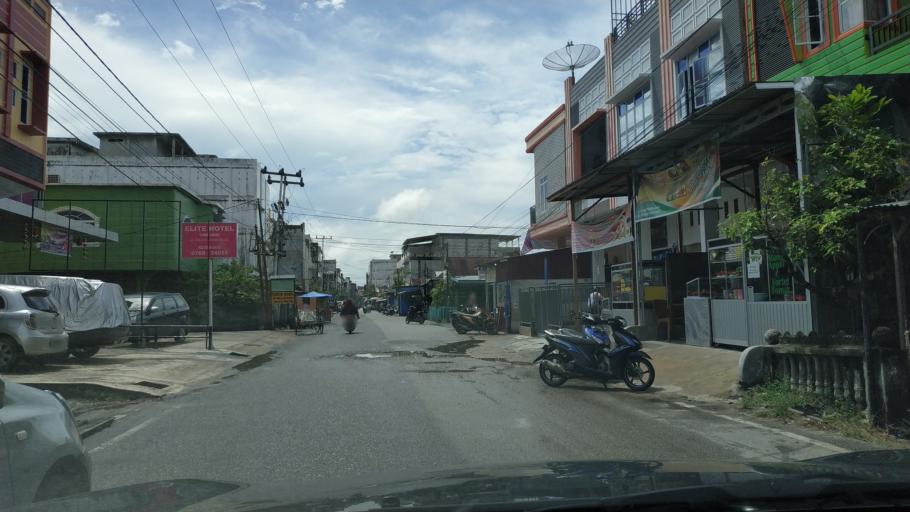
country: ID
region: Riau
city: Tembilahan
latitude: -0.3238
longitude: 103.1553
